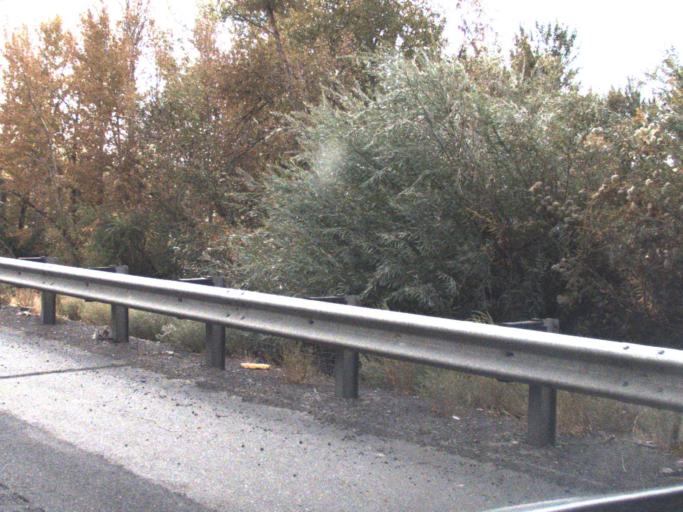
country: US
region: Washington
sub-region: Yakima County
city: Union Gap
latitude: 46.5251
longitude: -120.4708
